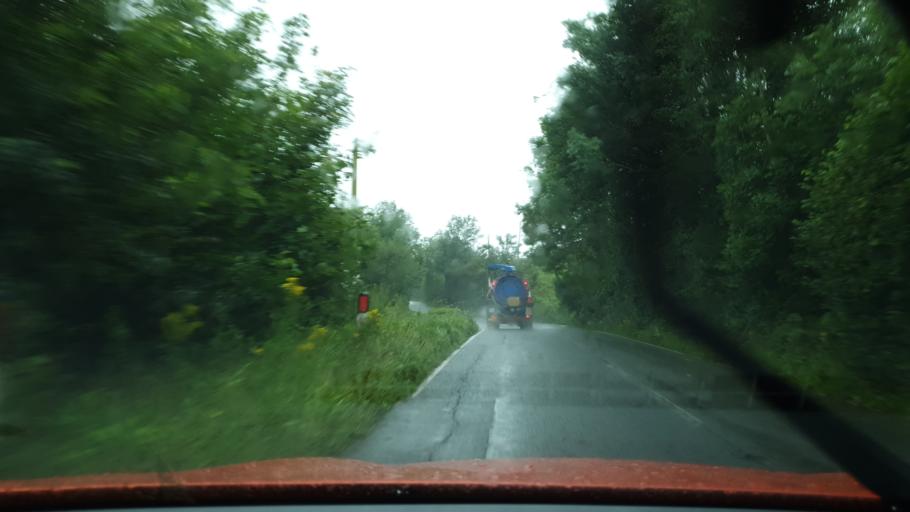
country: GB
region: England
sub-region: Cumbria
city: Askam in Furness
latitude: 54.2606
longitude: -3.2051
